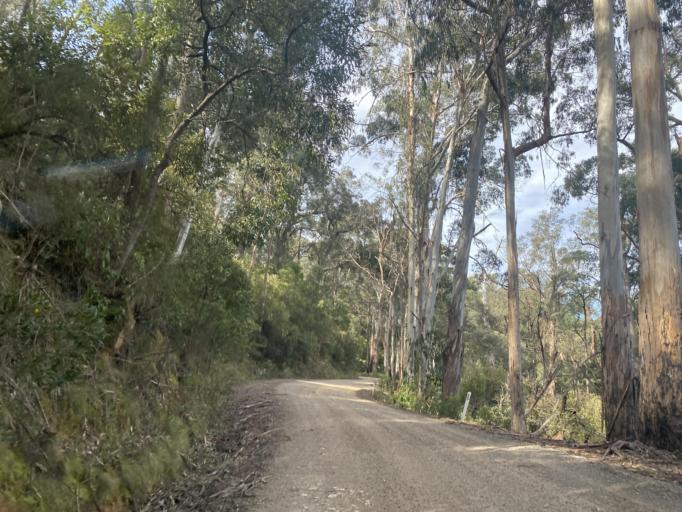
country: AU
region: Victoria
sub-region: Mansfield
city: Mansfield
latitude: -36.8446
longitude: 146.1717
